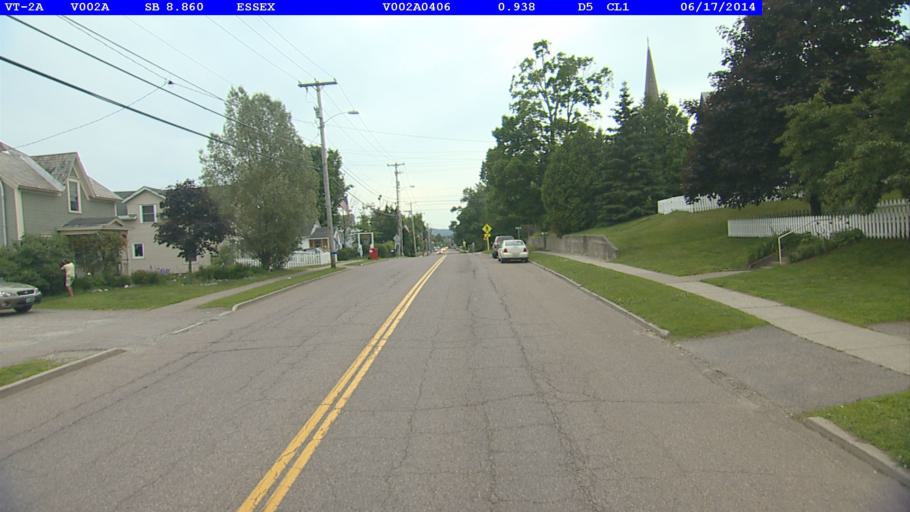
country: US
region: Vermont
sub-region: Chittenden County
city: Essex Junction
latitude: 44.4944
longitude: -73.1116
